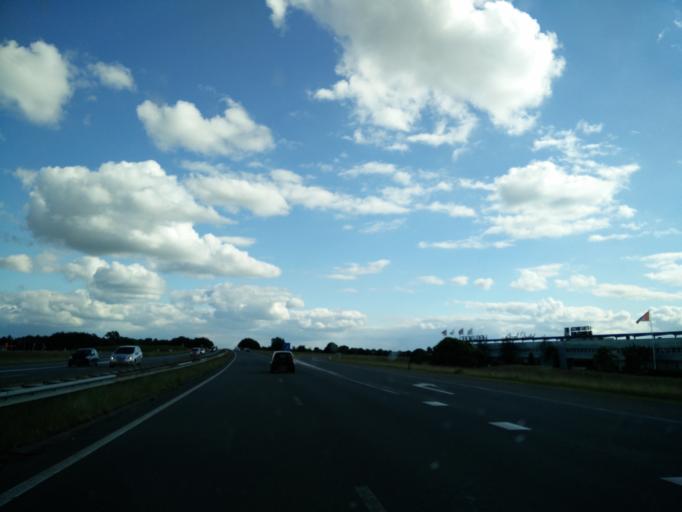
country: NL
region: Drenthe
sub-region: Gemeente Tynaarlo
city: Tynaarlo
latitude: 53.0848
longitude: 6.6040
